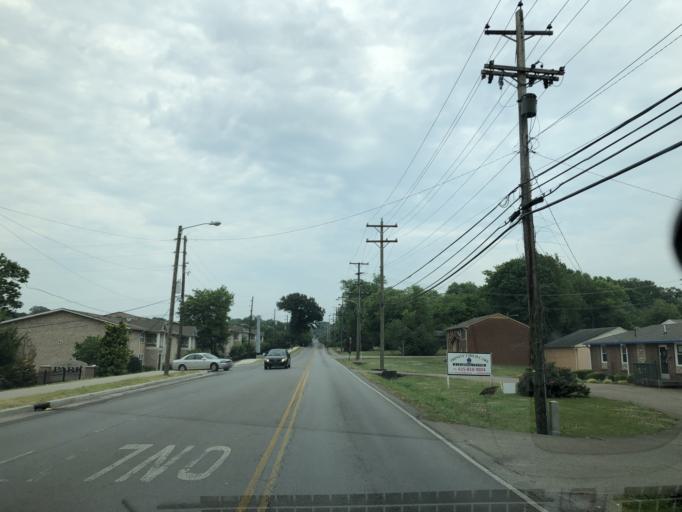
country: US
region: Tennessee
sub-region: Davidson County
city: Oak Hill
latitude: 36.0690
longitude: -86.6810
